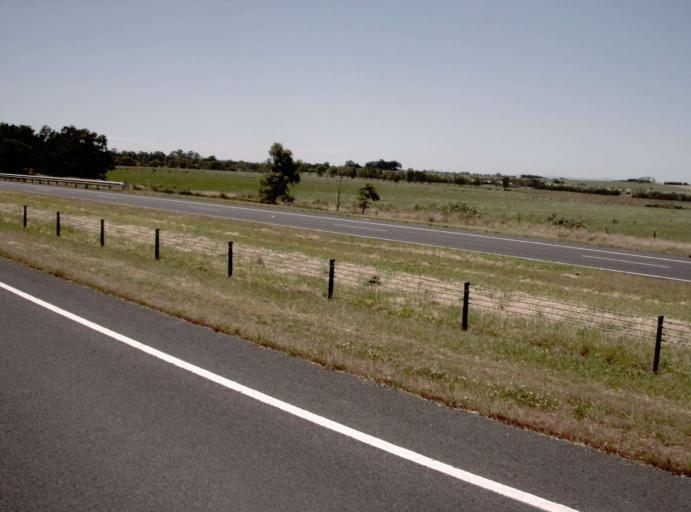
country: AU
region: Victoria
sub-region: Cardinia
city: Pakenham South
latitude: -38.0783
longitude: 145.5271
